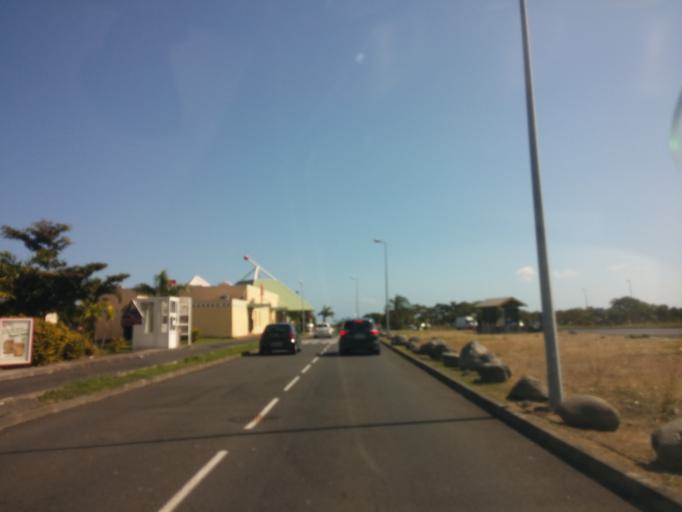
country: RE
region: Reunion
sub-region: Reunion
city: Le Port
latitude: -20.9550
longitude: 55.3098
